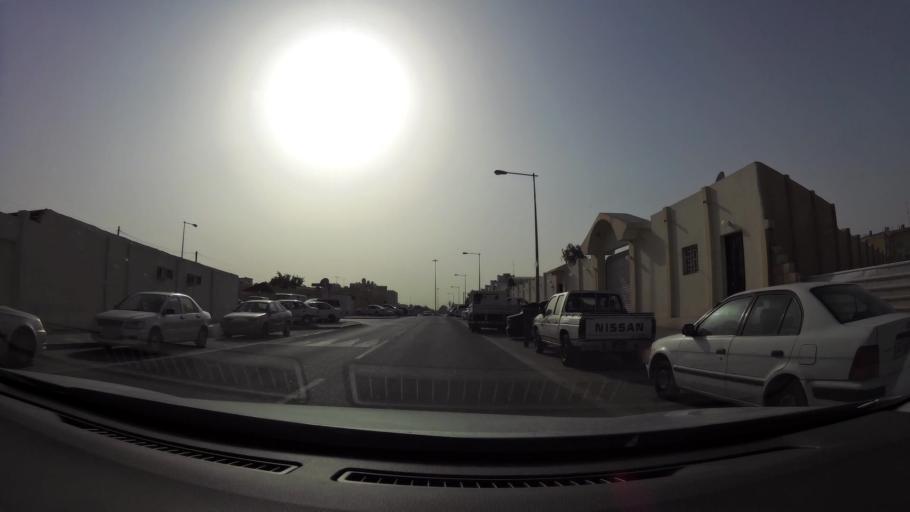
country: QA
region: Baladiyat ar Rayyan
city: Ar Rayyan
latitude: 25.2314
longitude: 51.4387
